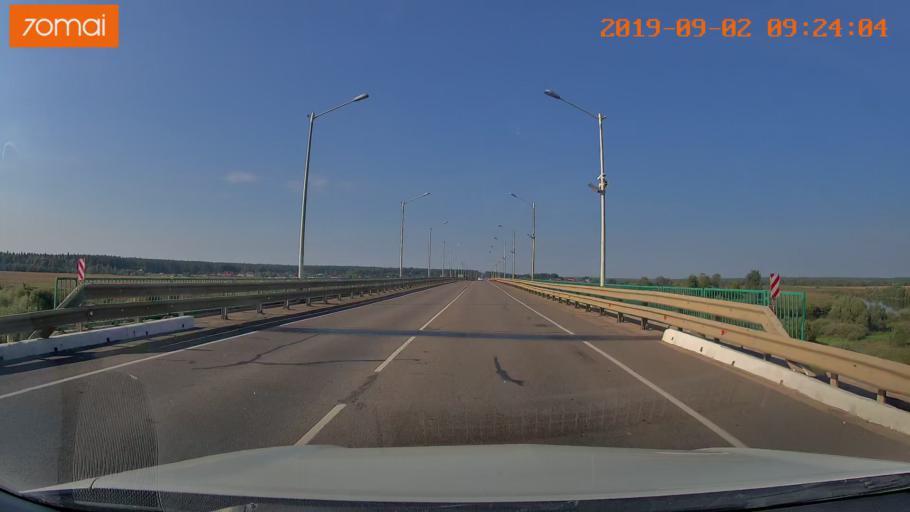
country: RU
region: Kaluga
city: Yukhnov
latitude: 54.7696
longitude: 35.3016
